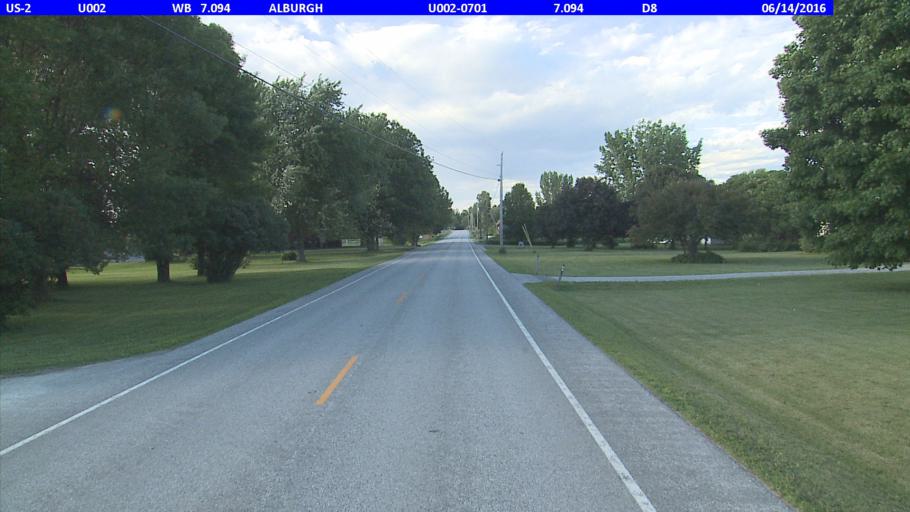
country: US
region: New York
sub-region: Clinton County
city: Rouses Point
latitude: 44.9487
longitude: -73.2726
